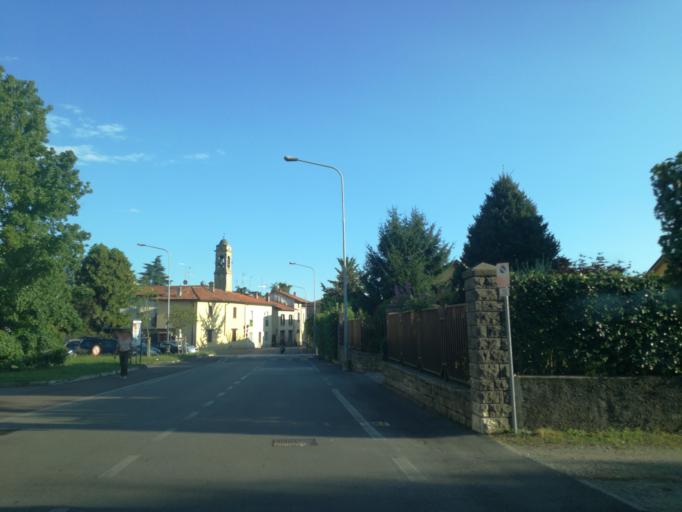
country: IT
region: Lombardy
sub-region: Provincia di Lecco
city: Robbiate
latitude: 45.6933
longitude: 9.4415
